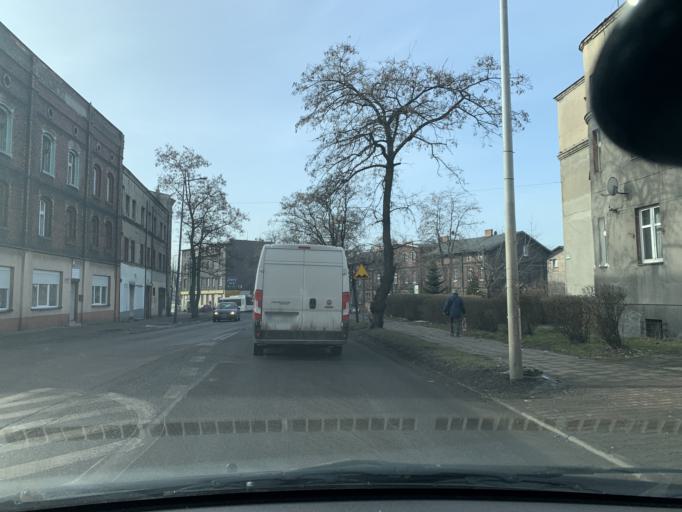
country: PL
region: Silesian Voivodeship
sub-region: Bytom
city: Bytom
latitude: 50.3391
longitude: 18.8694
